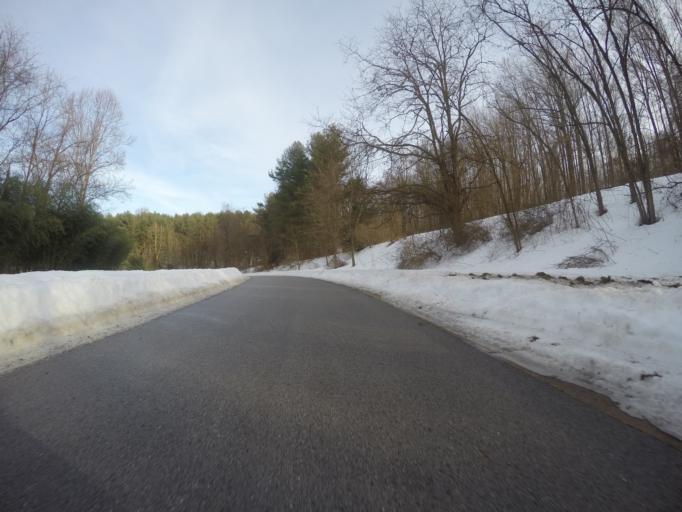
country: US
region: Maryland
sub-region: Baltimore County
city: Hunt Valley
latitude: 39.5594
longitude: -76.6188
